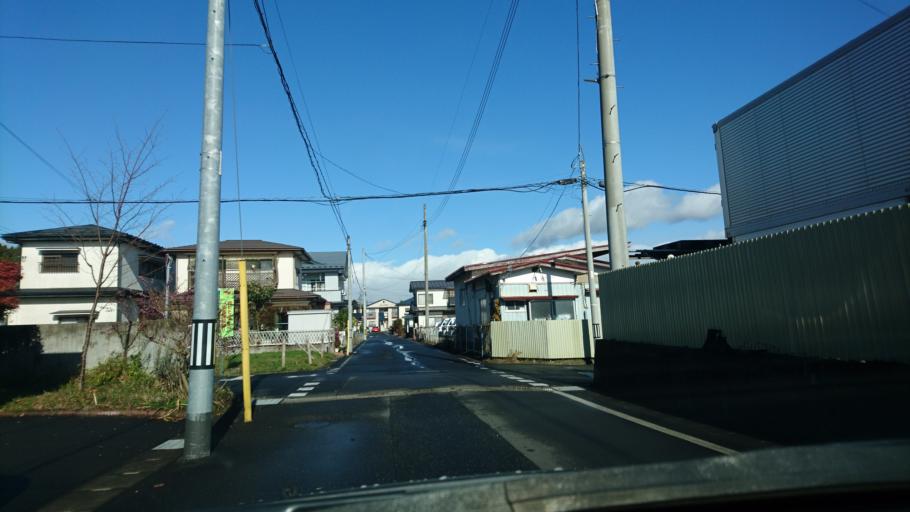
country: JP
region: Iwate
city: Ichinoseki
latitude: 38.9417
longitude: 141.1281
